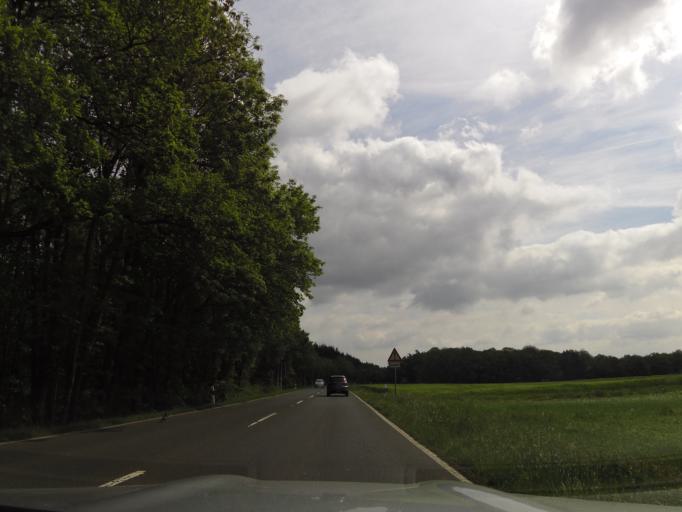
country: DE
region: Hesse
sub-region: Regierungsbezirk Giessen
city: Wetzlar
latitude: 50.5535
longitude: 8.5428
